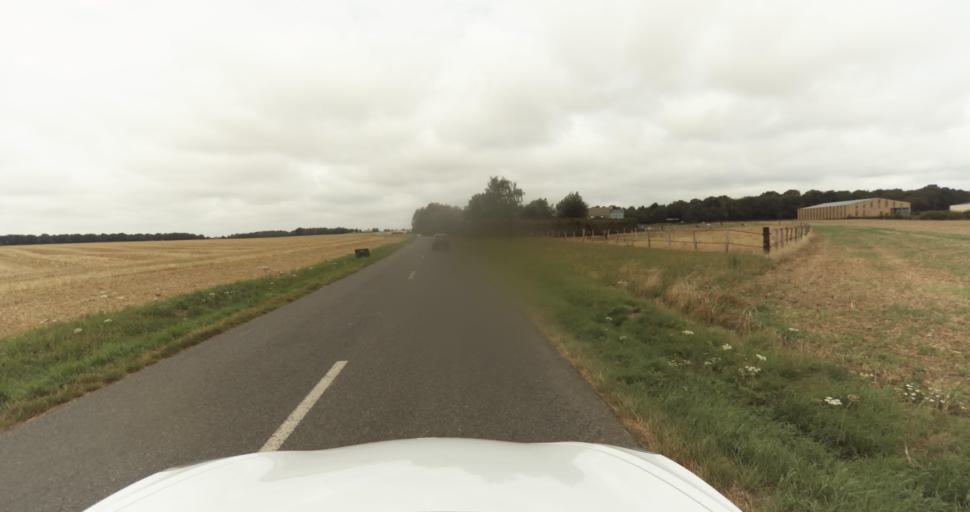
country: FR
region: Haute-Normandie
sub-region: Departement de l'Eure
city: Aviron
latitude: 49.0567
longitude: 1.0857
